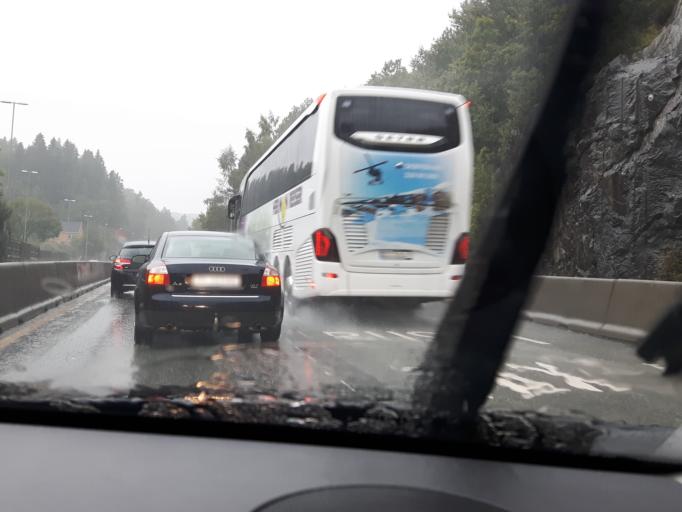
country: NO
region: Vest-Agder
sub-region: Kristiansand
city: Strai
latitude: 58.1441
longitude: 7.9300
